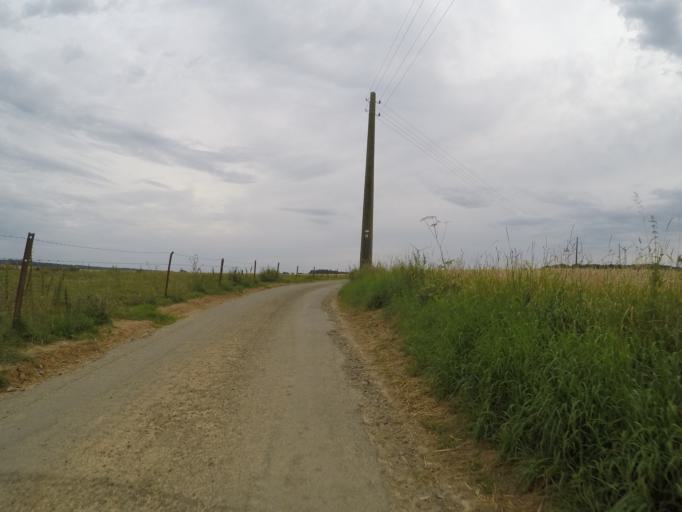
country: BE
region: Wallonia
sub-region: Province de Namur
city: Assesse
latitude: 50.3043
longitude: 5.0001
